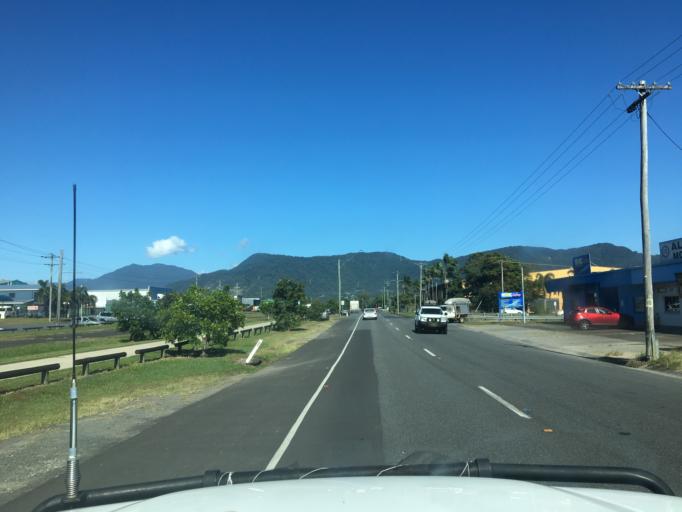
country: AU
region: Queensland
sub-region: Cairns
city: Woree
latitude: -16.9380
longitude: 145.7590
